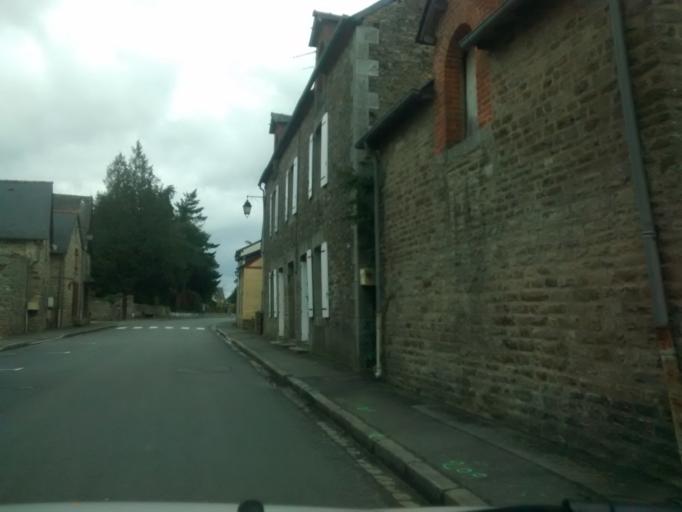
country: FR
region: Brittany
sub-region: Departement d'Ille-et-Vilaine
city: Livre-sur-Changeon
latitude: 48.2203
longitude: -1.3450
